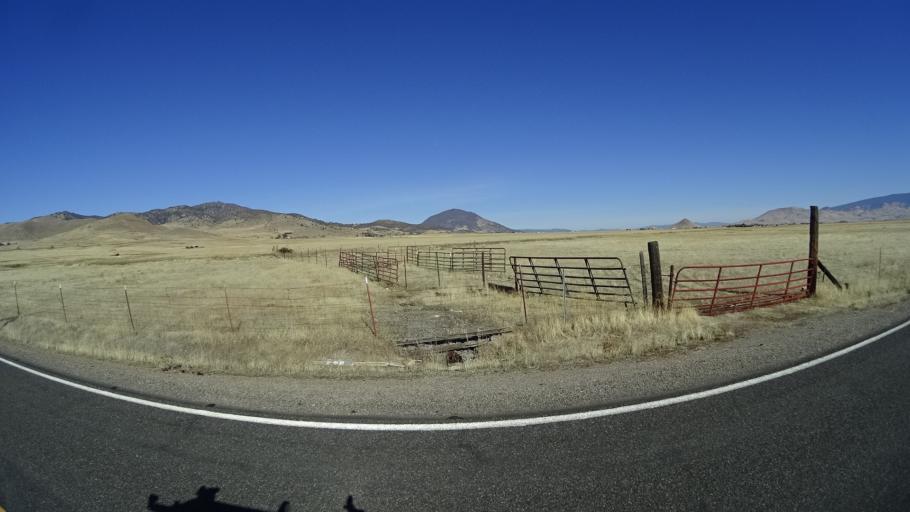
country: US
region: California
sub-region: Siskiyou County
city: Montague
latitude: 41.7707
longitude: -122.5110
